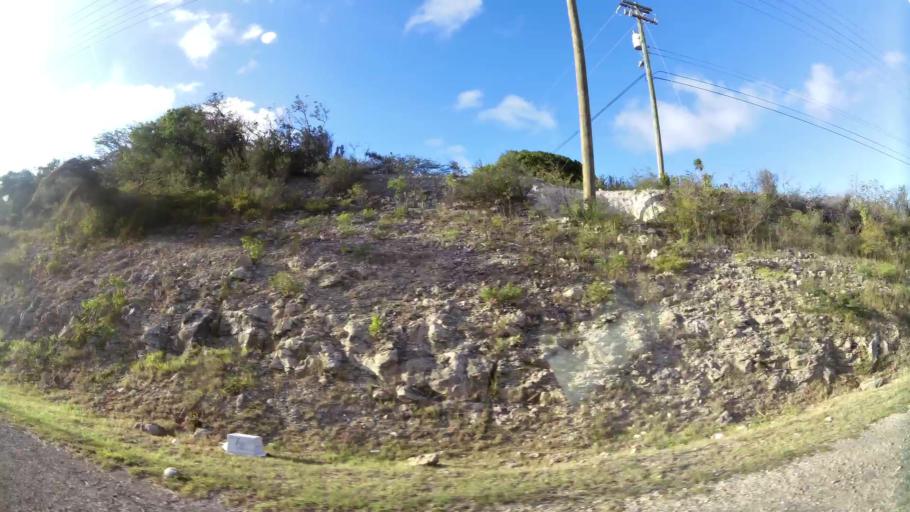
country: AG
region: Saint George
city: Piggotts
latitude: 17.1341
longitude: -61.8004
